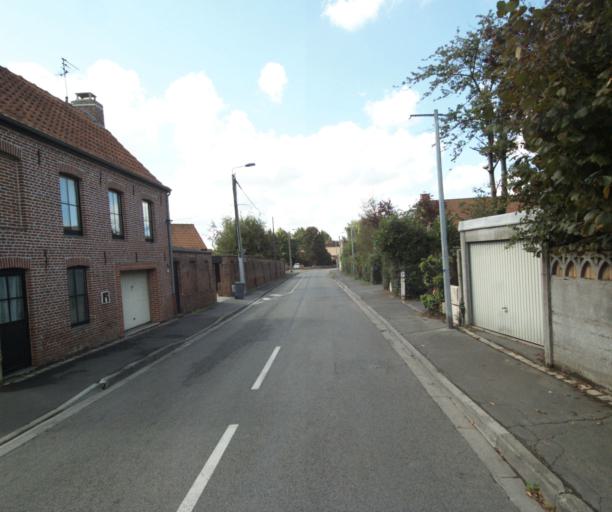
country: FR
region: Nord-Pas-de-Calais
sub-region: Departement du Nord
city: Willems
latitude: 50.6313
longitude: 3.2353
